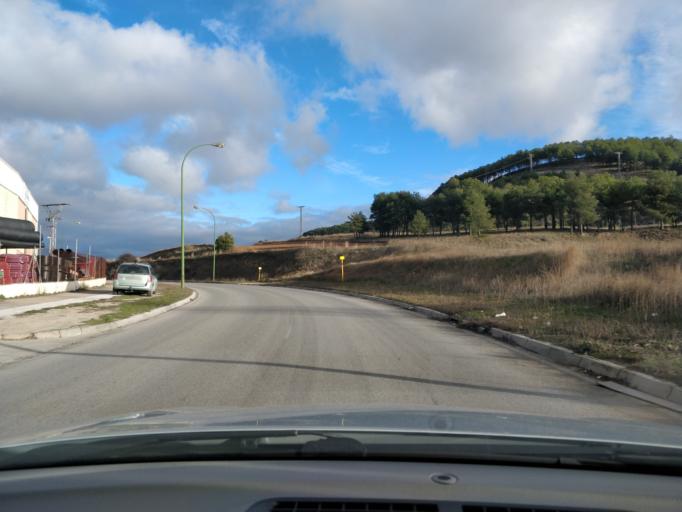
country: ES
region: Castille and Leon
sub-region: Provincia de Burgos
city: Villalbilla de Burgos
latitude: 42.3630
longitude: -3.7508
